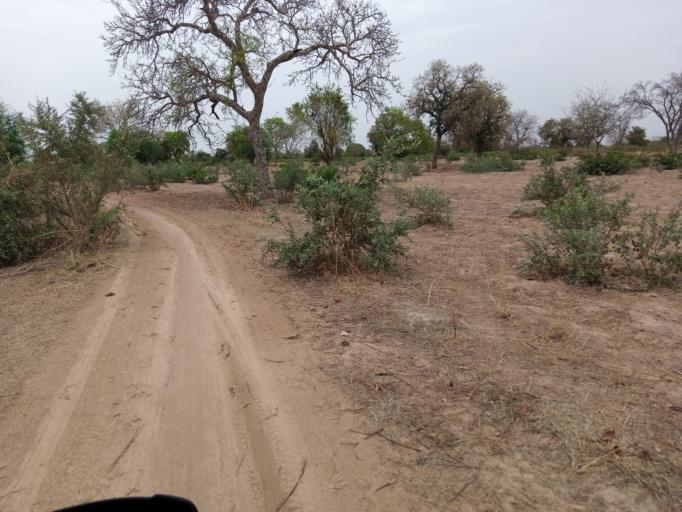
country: BF
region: Boucle du Mouhoun
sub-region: Province de la Kossi
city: Nouna
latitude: 12.8307
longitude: -4.0771
